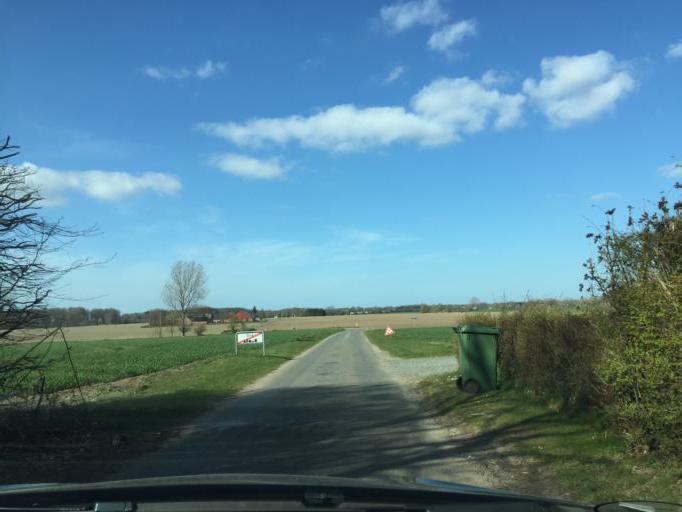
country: DK
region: South Denmark
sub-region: Faaborg-Midtfyn Kommune
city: Arslev
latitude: 55.2977
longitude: 10.5183
